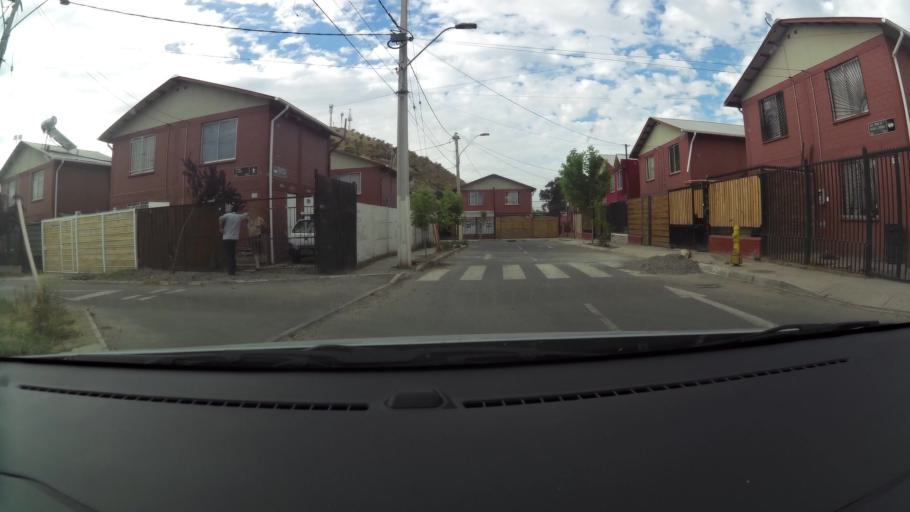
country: CL
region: Santiago Metropolitan
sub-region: Provincia de Cordillera
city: Puente Alto
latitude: -33.6284
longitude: -70.6017
